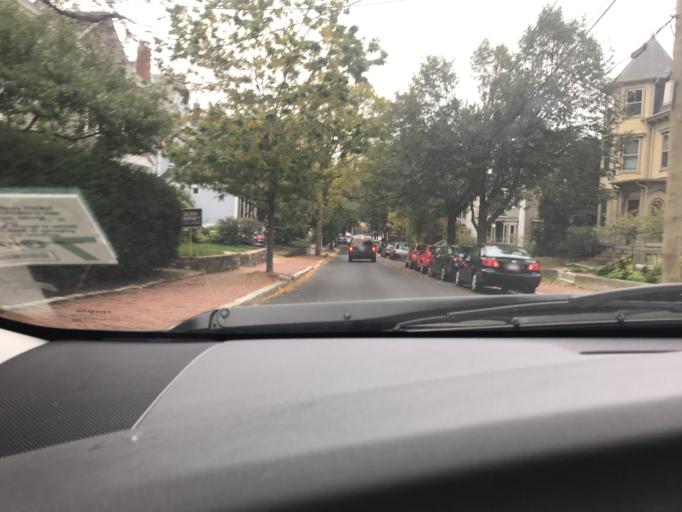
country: US
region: Massachusetts
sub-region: Middlesex County
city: Cambridge
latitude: 42.3863
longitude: -71.1215
